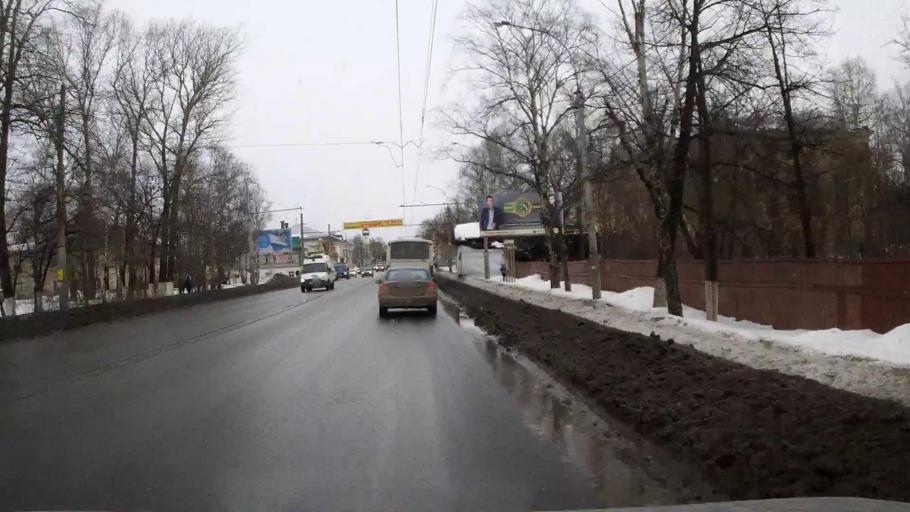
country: RU
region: Vologda
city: Vologda
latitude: 59.2252
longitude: 39.8925
